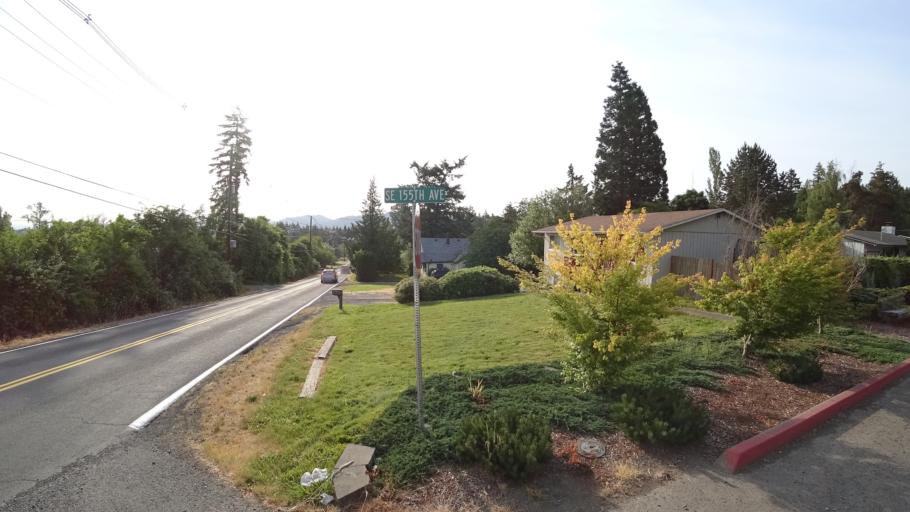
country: US
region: Oregon
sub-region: Clackamas County
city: Happy Valley
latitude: 45.4611
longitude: -122.5037
